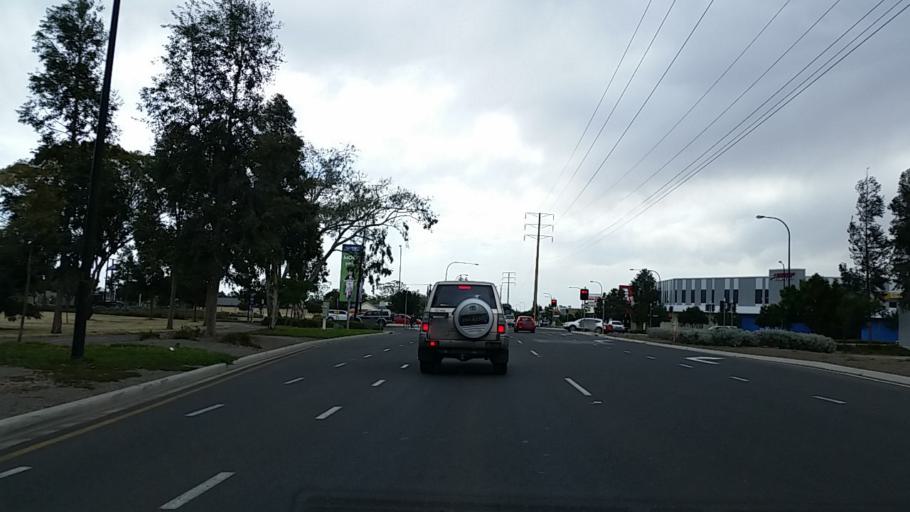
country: AU
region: South Australia
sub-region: Playford
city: Smithfield
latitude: -34.6723
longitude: 138.6802
